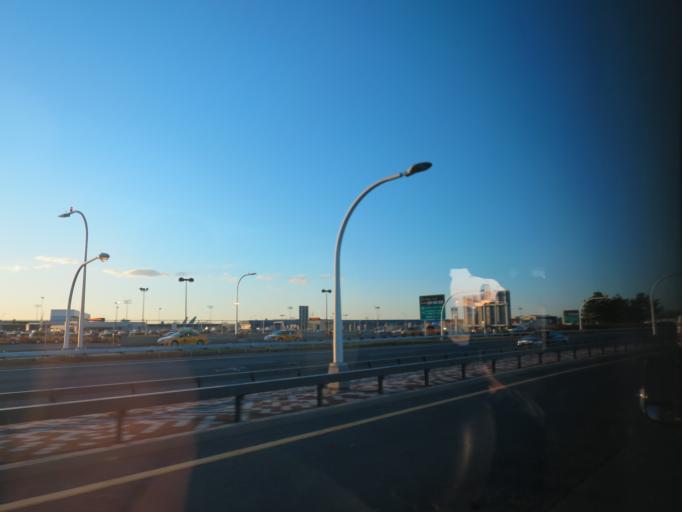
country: US
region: New York
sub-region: Queens County
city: Jamaica
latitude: 40.6570
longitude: -73.7926
